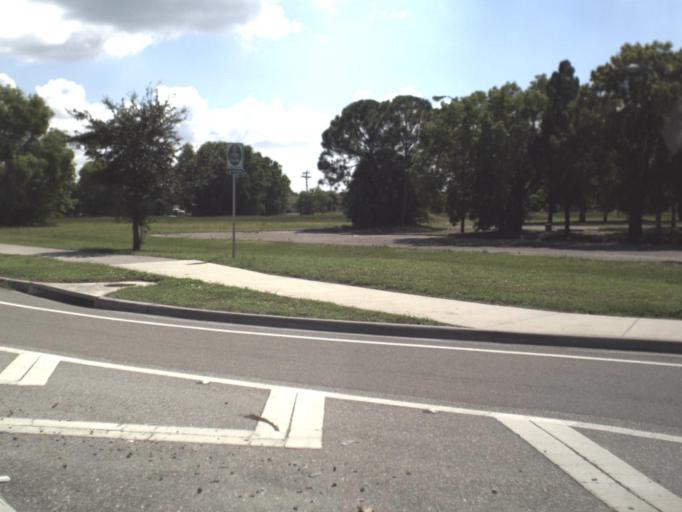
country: US
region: Florida
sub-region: Lee County
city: Cape Coral
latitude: 26.6041
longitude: -81.9740
